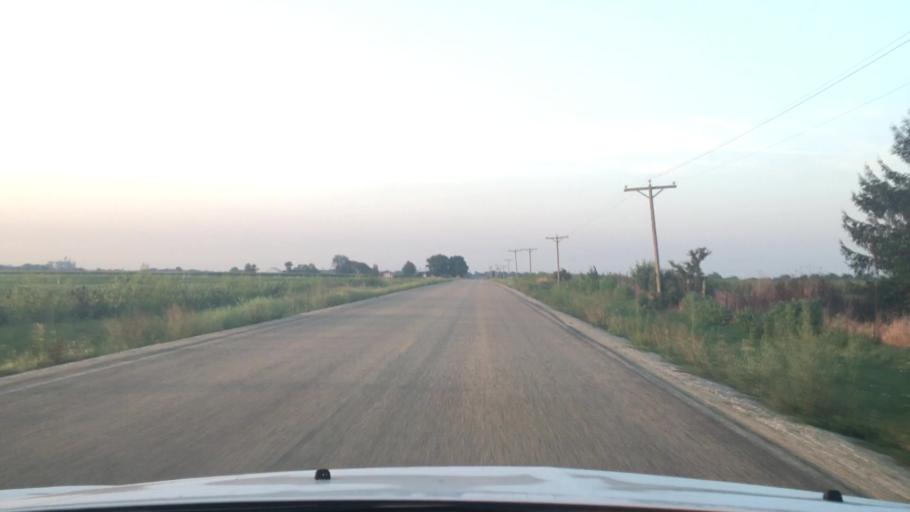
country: US
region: Illinois
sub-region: DeKalb County
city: Waterman
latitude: 41.7951
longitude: -88.7738
